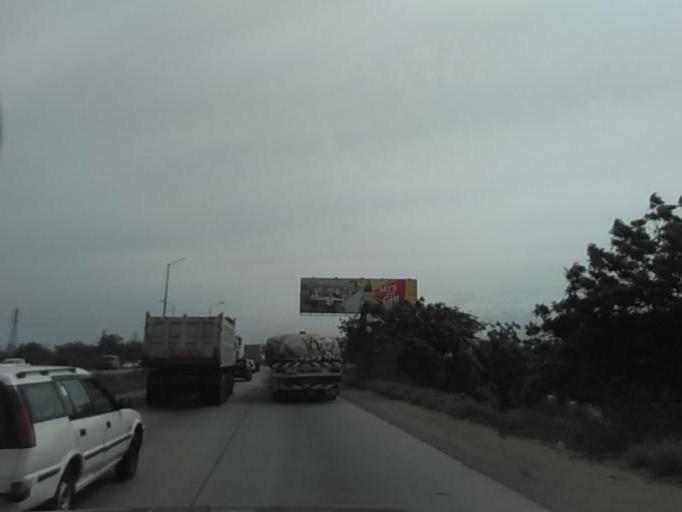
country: GH
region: Greater Accra
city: Tema
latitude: 5.6755
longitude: -0.0428
